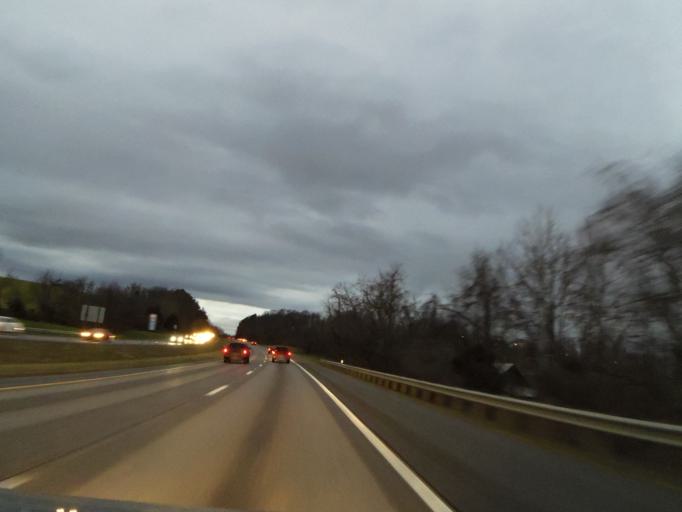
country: US
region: Tennessee
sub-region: Washington County
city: Oak Grove
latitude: 36.3691
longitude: -82.4152
